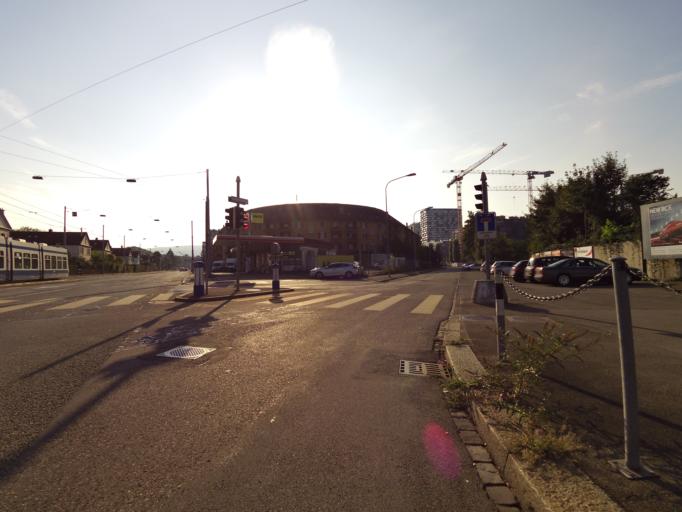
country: CH
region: Zurich
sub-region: Bezirk Zuerich
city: Zuerich (Kreis 5) / Escher-Wyss
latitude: 47.3937
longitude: 8.5057
